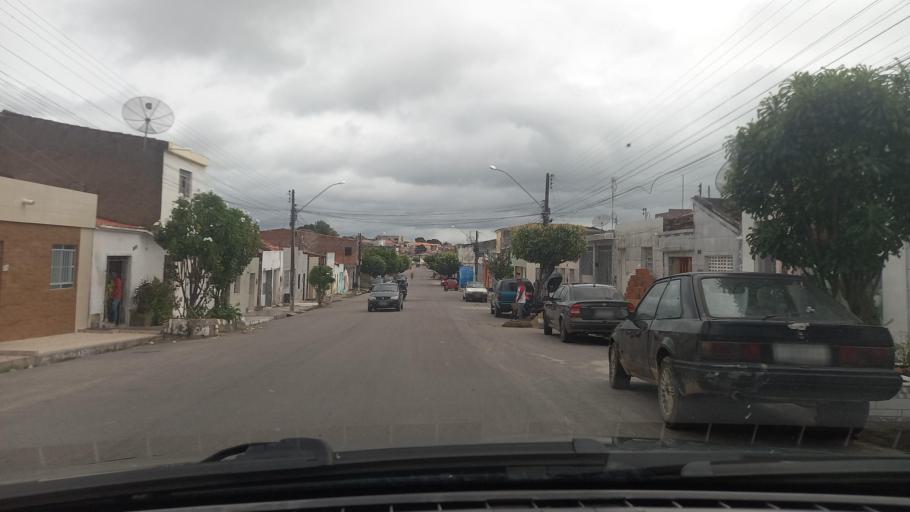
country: BR
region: Alagoas
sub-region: Delmiro Gouveia
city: Delmiro Gouveia
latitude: -9.3844
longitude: -38.0010
